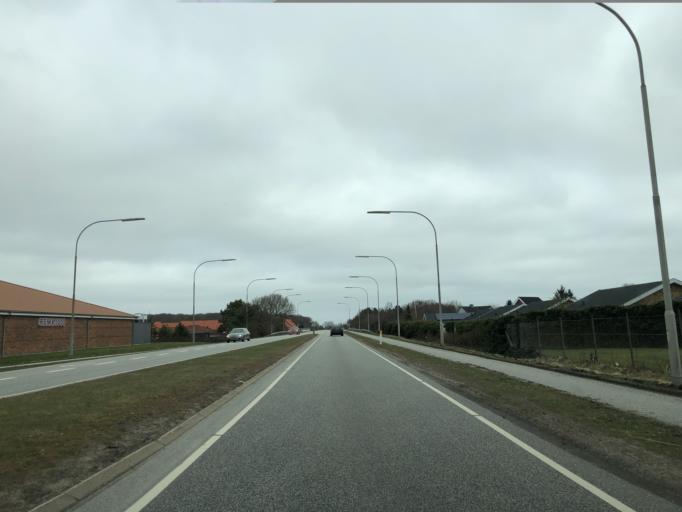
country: DK
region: North Denmark
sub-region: Frederikshavn Kommune
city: Saeby
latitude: 57.3313
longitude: 10.5057
